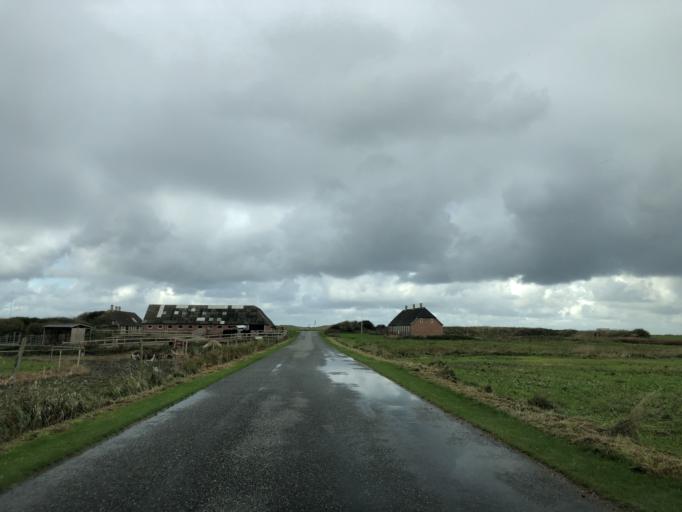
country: DK
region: Central Jutland
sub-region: Lemvig Kommune
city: Harboore
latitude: 56.4738
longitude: 8.1351
